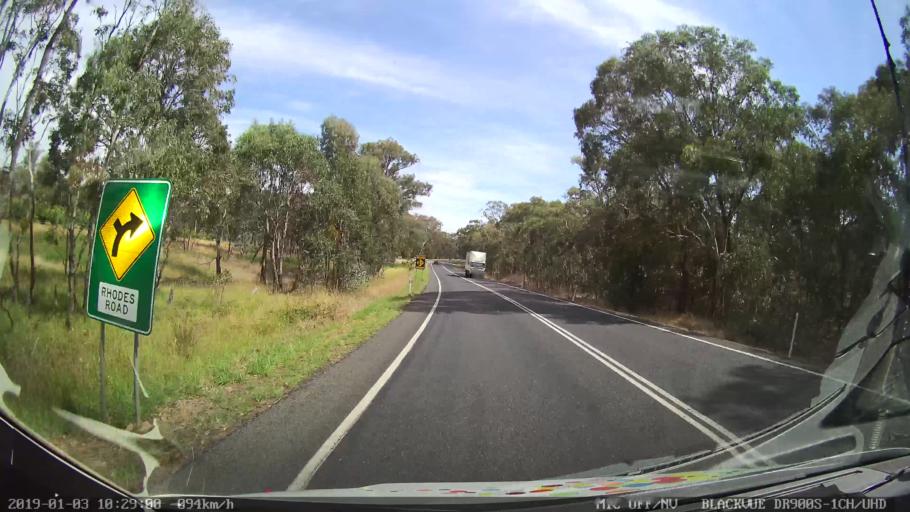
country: AU
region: New South Wales
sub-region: Young
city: Young
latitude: -34.3799
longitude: 148.2601
